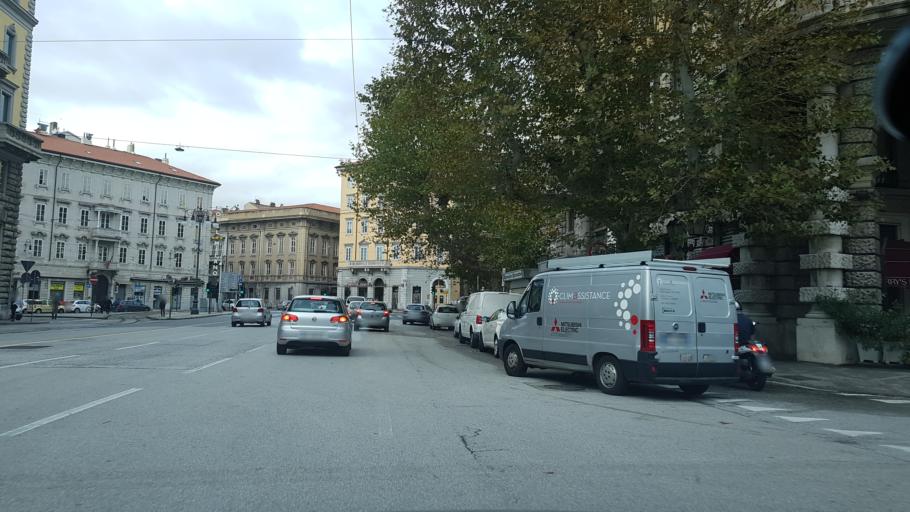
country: IT
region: Friuli Venezia Giulia
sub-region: Provincia di Trieste
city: Trieste
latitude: 45.6544
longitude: 13.7757
